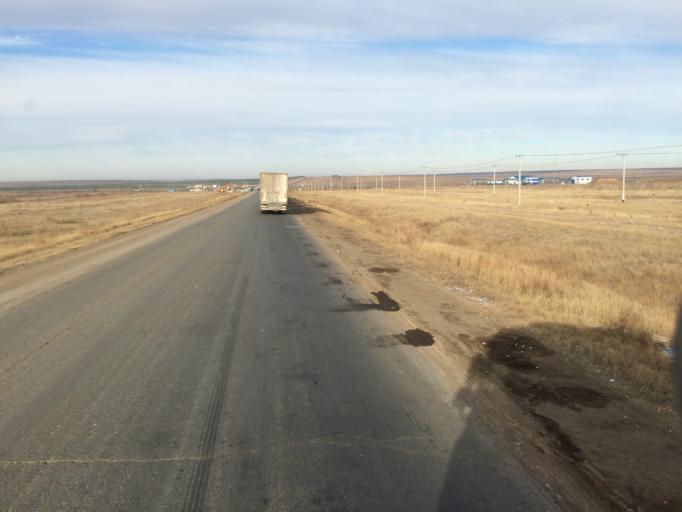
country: KZ
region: Batys Qazaqstan
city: Peremetnoe
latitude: 51.6597
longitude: 51.0085
